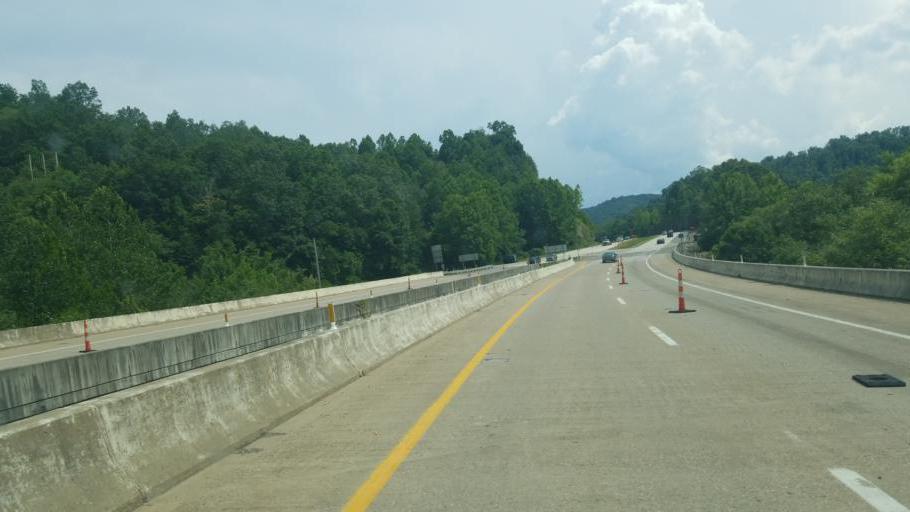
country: US
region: West Virginia
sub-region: Kanawha County
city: Alum Creek
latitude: 38.2225
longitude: -81.8349
